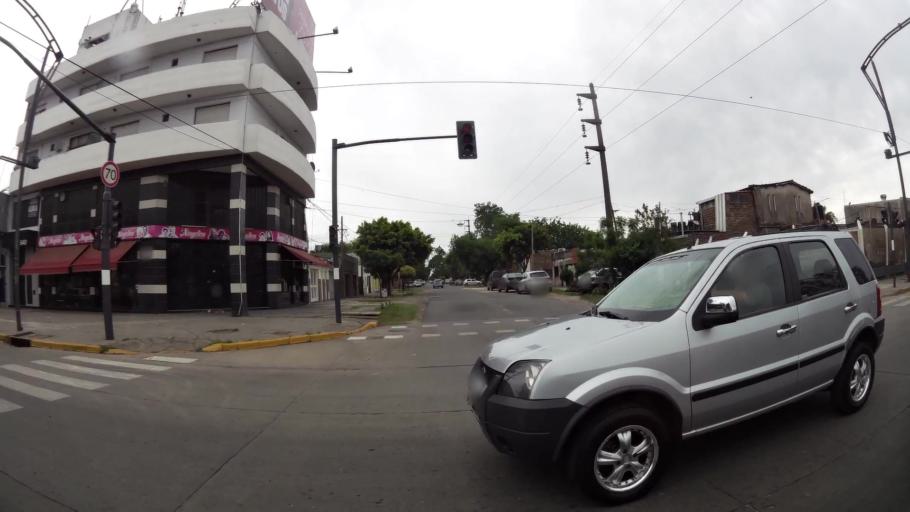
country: AR
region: Santa Fe
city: Gobernador Galvez
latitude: -33.0007
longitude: -60.6653
